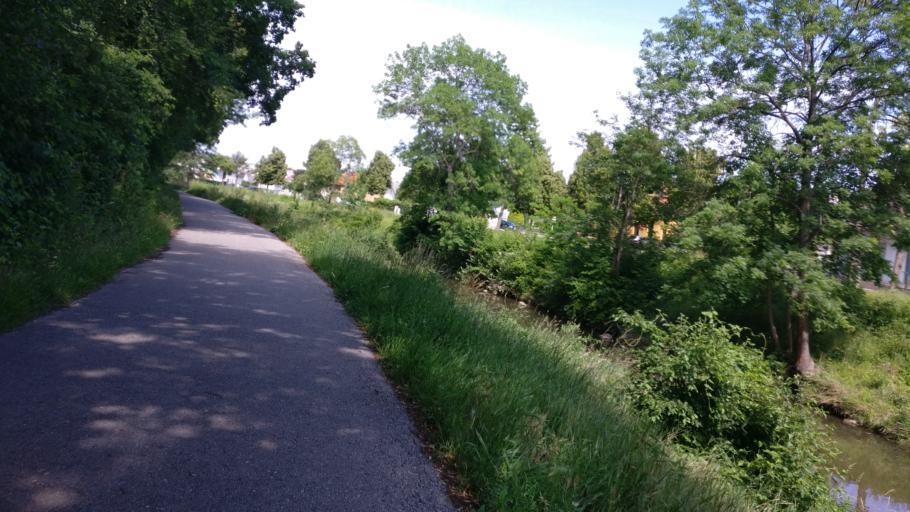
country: AT
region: Lower Austria
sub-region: Politischer Bezirk Baden
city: Oberwaltersdorf
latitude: 47.9716
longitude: 16.3202
